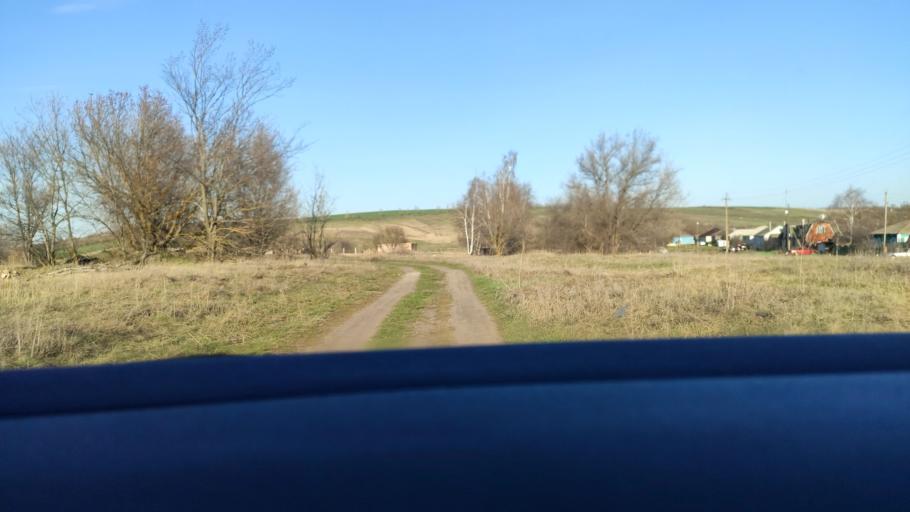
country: RU
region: Voronezj
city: Uryv-Pokrovka
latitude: 51.1480
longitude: 39.0223
